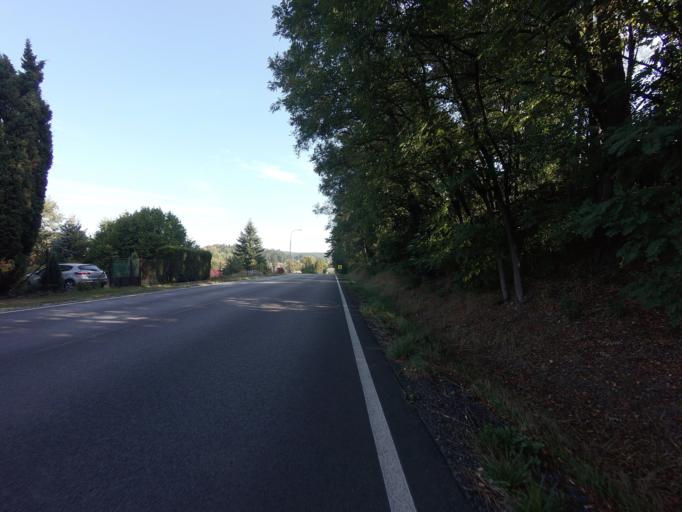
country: CZ
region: Jihocesky
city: Tyn nad Vltavou
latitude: 49.2499
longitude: 14.4213
